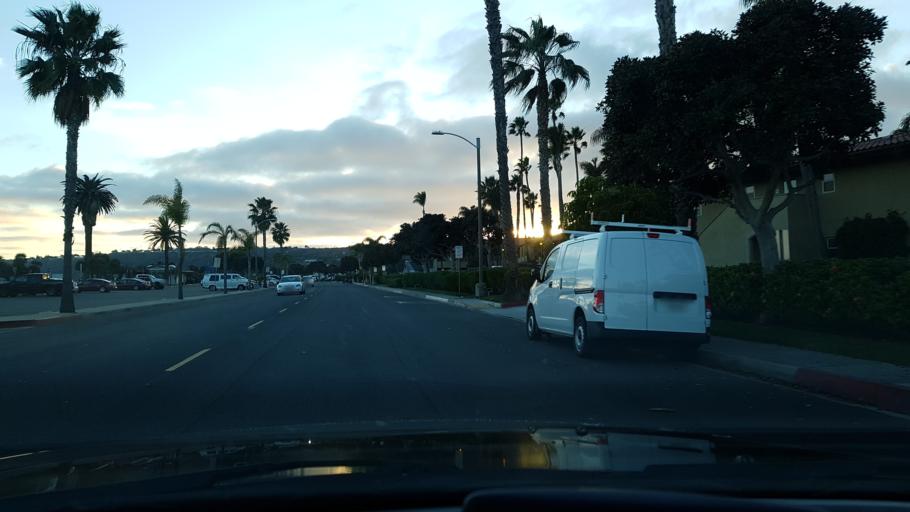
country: US
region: California
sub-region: San Diego County
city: Coronado
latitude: 32.7130
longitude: -117.2278
